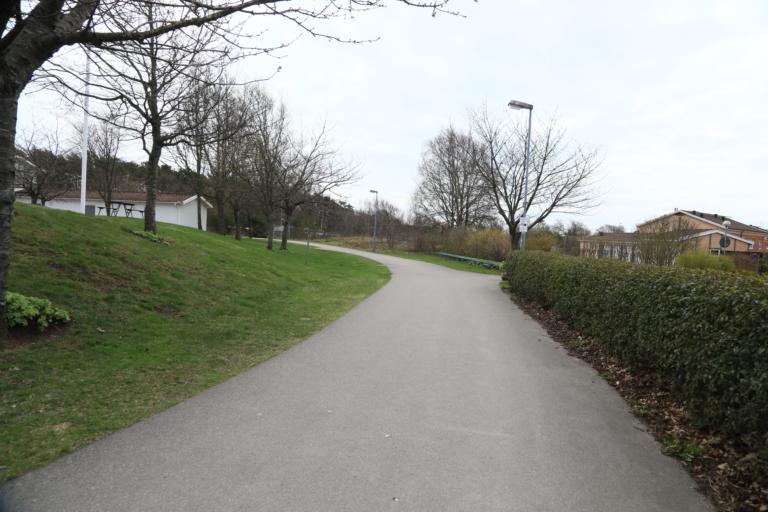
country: SE
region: Halland
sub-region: Varbergs Kommun
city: Varberg
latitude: 57.0904
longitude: 12.2608
